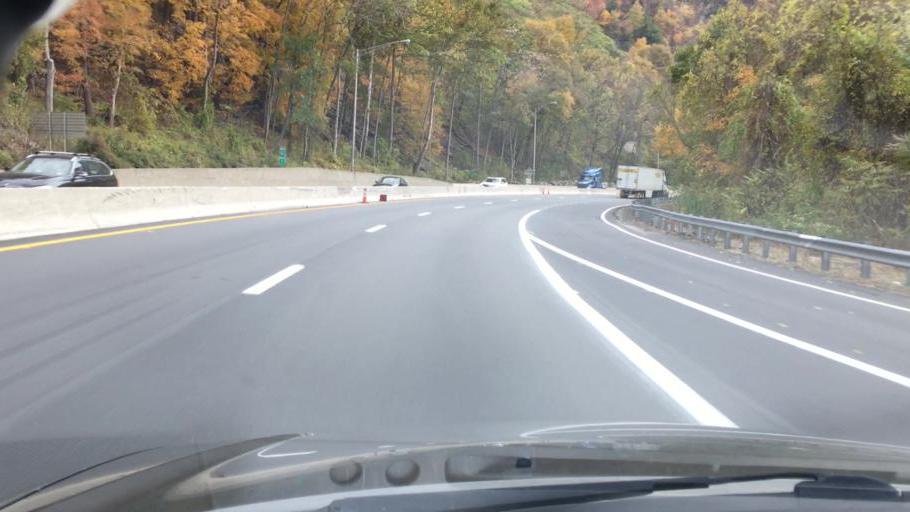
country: US
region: Pennsylvania
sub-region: Monroe County
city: East Stroudsburg
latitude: 40.9720
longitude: -75.1190
